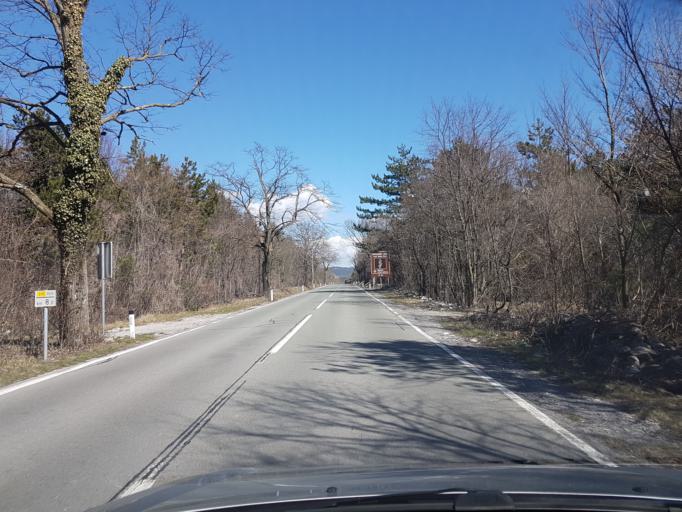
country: SI
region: Sezana
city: Sezana
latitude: 45.6559
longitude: 13.8836
